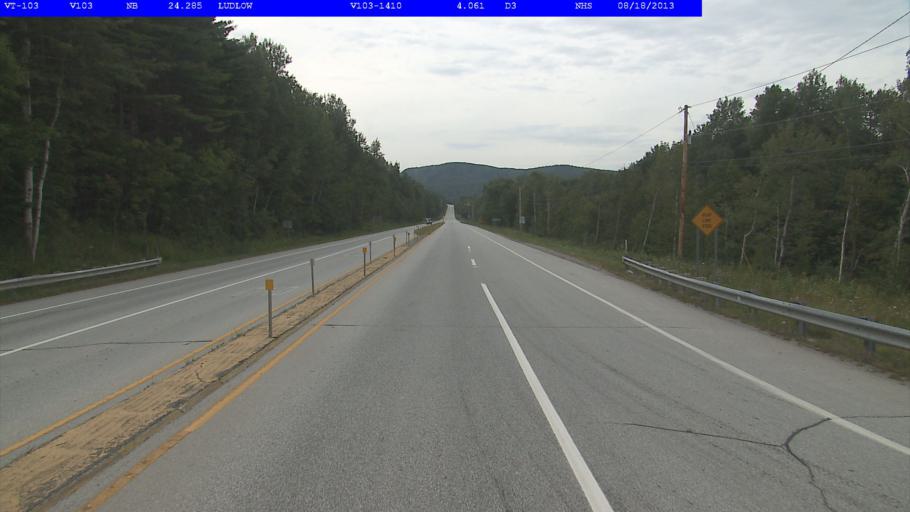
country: US
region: Vermont
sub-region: Windsor County
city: Chester
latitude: 43.4200
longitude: -72.7071
